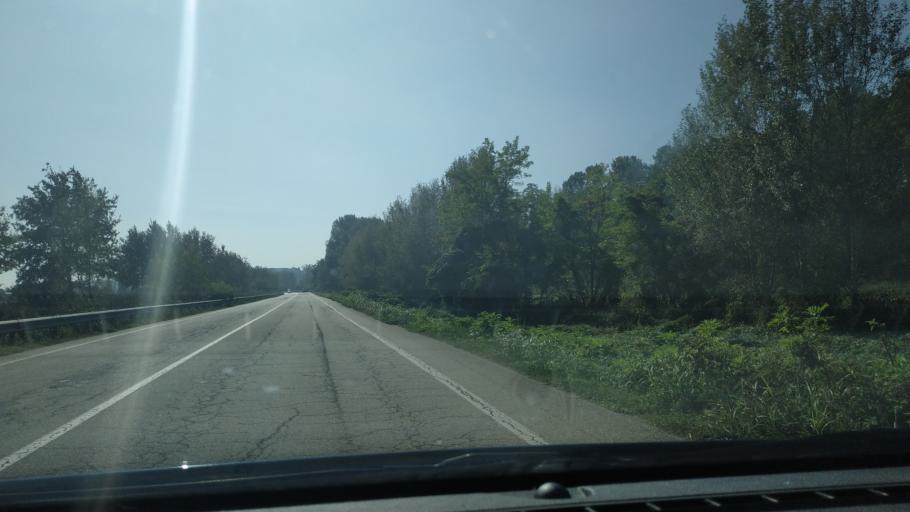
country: IT
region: Piedmont
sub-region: Provincia di Alessandria
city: Valenza
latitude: 45.0348
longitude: 8.6286
